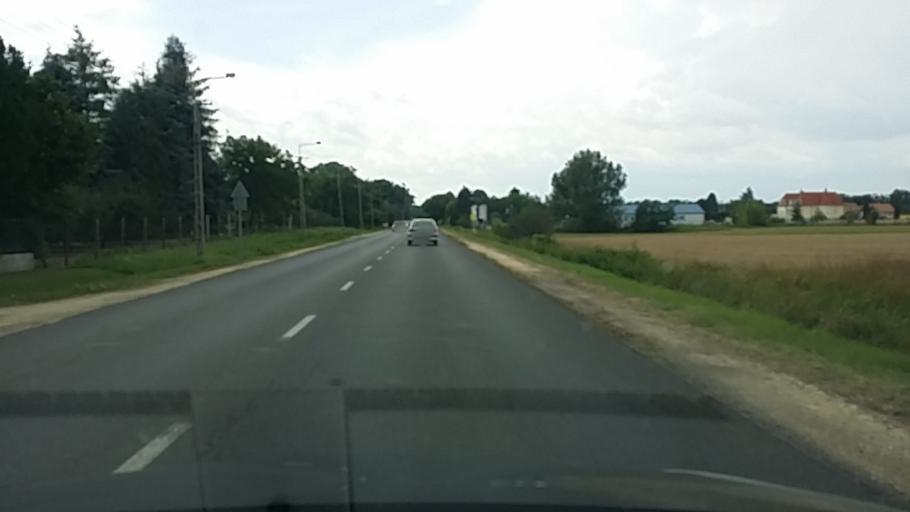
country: HU
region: Pest
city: Orkeny
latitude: 47.1217
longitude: 19.4379
